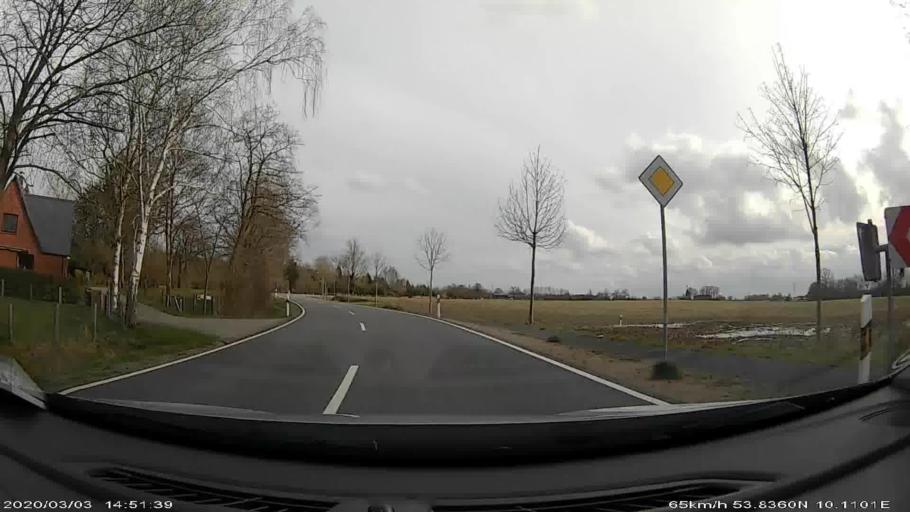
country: DE
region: Schleswig-Holstein
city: Sievershutten
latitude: 53.8362
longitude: 10.1099
